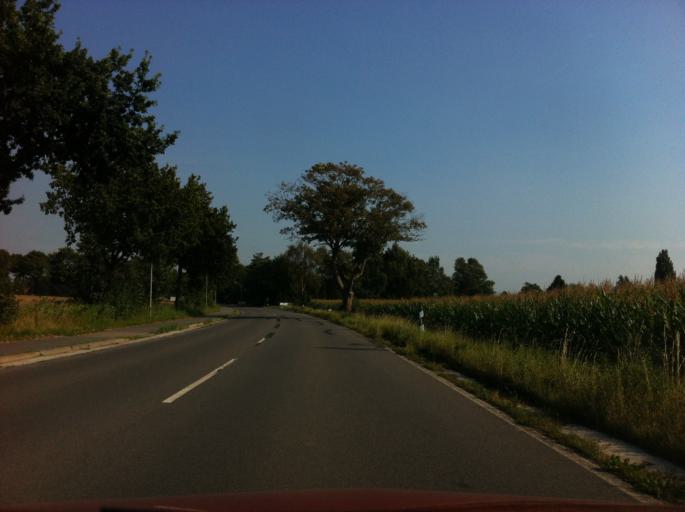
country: DE
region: Schleswig-Holstein
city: Oldenburg in Holstein
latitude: 54.2989
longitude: 10.8602
